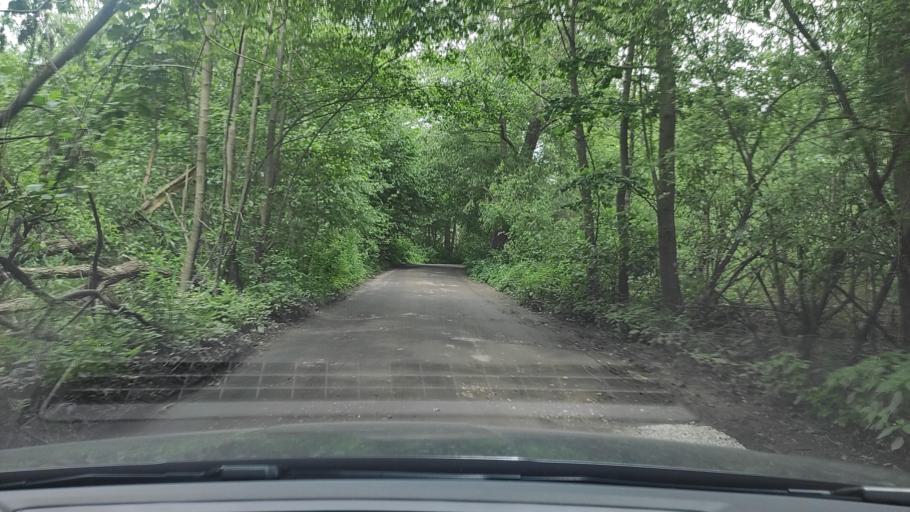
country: PL
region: Greater Poland Voivodeship
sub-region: Powiat poznanski
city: Pobiedziska
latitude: 52.5040
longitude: 17.2039
